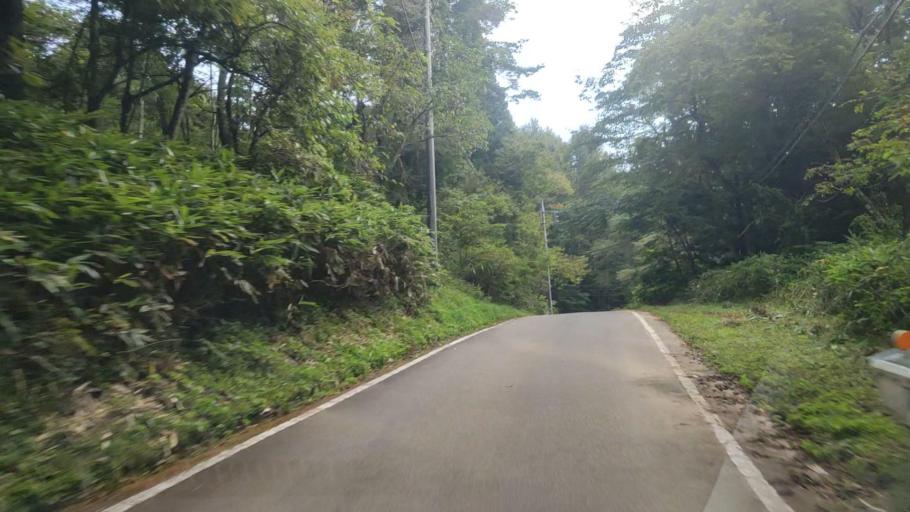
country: JP
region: Gunma
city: Nakanojomachi
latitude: 36.6567
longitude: 138.6336
